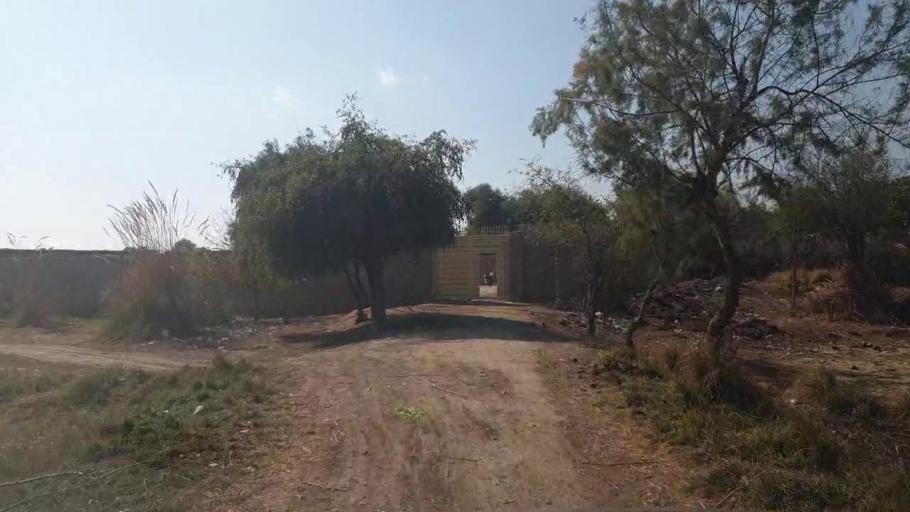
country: PK
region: Sindh
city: Shahdadpur
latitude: 25.9256
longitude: 68.5714
